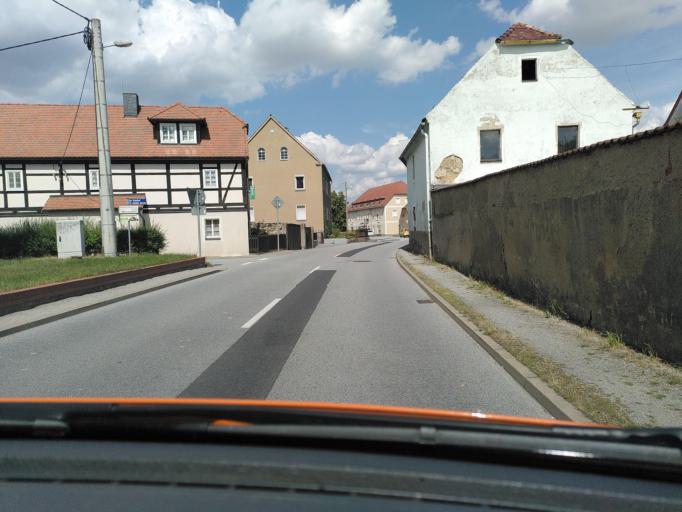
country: DE
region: Saxony
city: Grossdubrau
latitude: 51.2259
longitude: 14.4783
